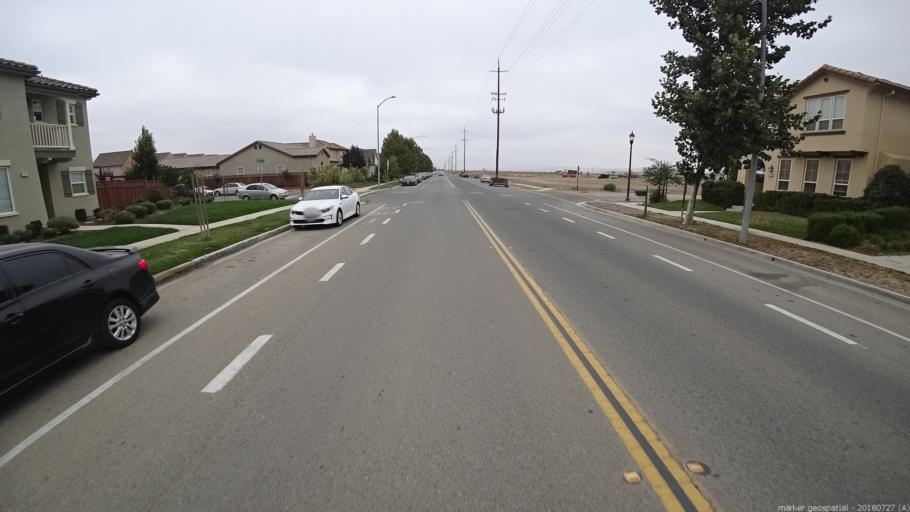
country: US
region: California
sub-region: Monterey County
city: King City
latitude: 36.2201
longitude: -121.1323
